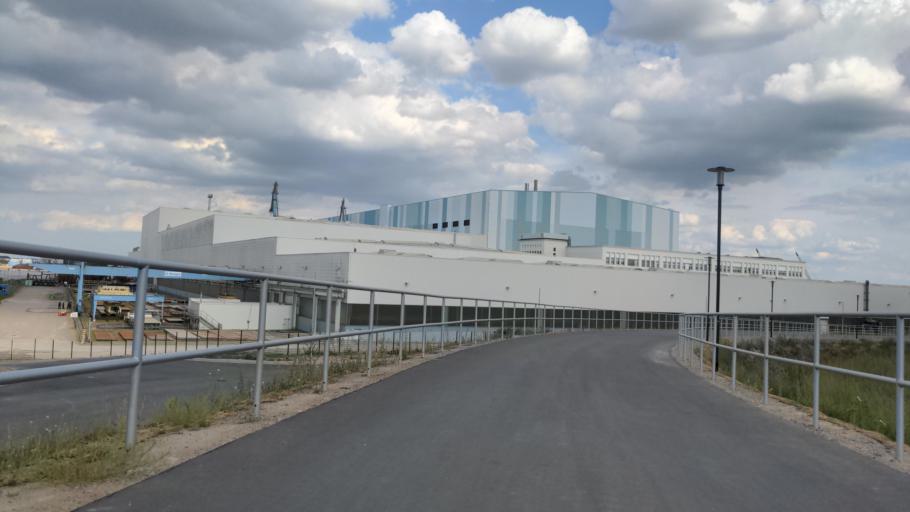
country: DE
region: Mecklenburg-Vorpommern
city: Wismar
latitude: 53.8981
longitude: 11.4302
